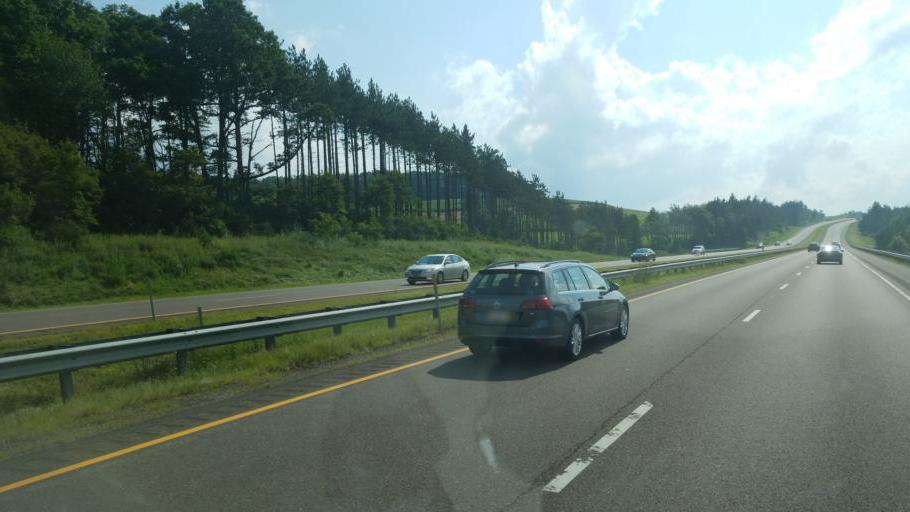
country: US
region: Maryland
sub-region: Allegany County
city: Frostburg
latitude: 39.6866
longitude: -78.9859
